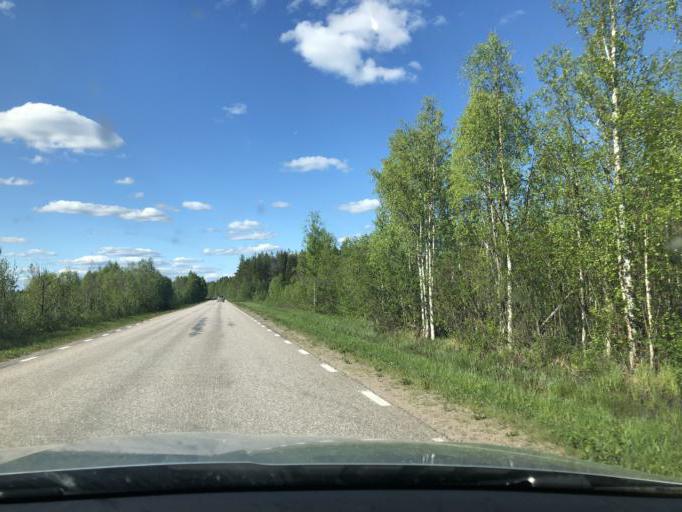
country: SE
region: Norrbotten
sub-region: Kalix Kommun
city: Kalix
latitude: 65.9139
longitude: 23.1733
